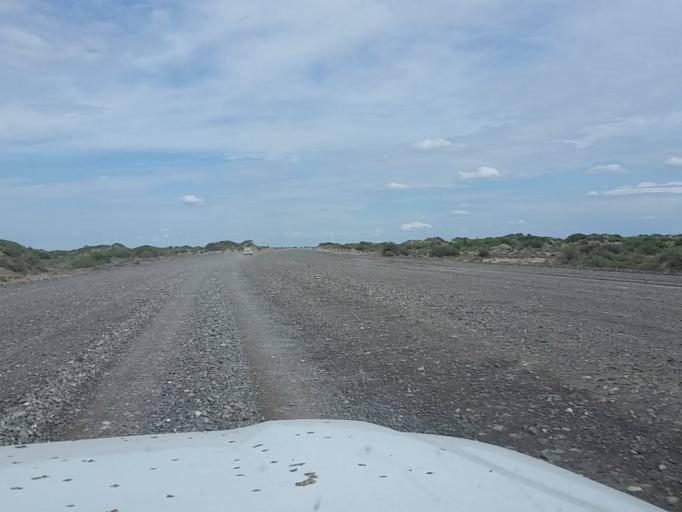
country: KZ
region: Almaty Oblysy
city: Zharkent
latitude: 43.8656
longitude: 79.3720
